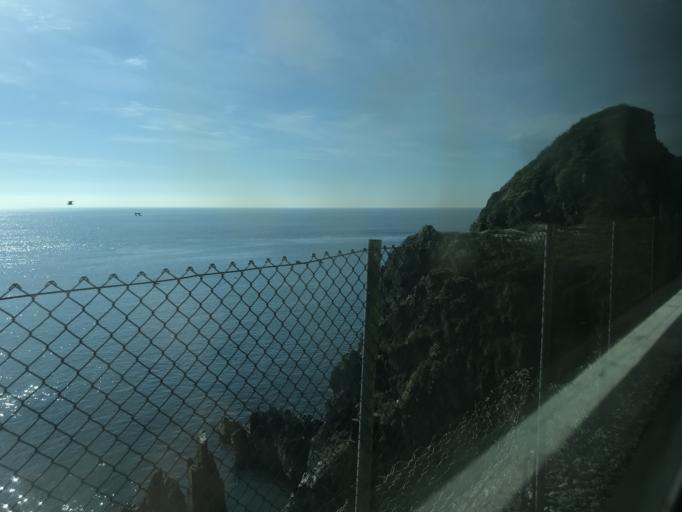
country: IE
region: Leinster
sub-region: Wicklow
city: Bray
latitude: 53.1795
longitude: -6.0753
